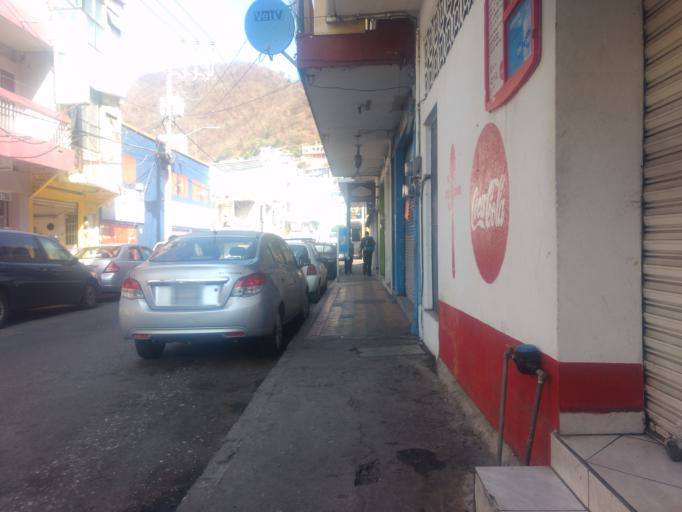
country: MX
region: Colima
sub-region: Manzanillo
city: Manzanillo
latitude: 19.0512
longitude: -104.3169
